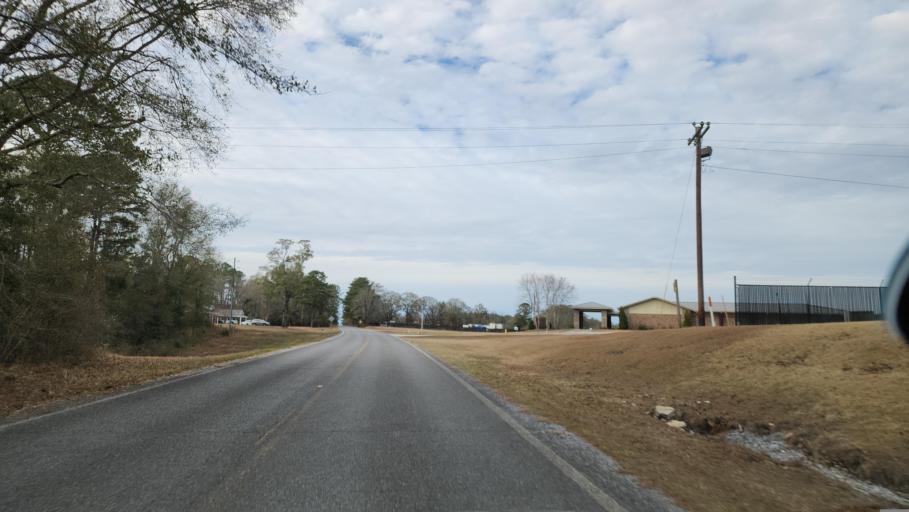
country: US
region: Mississippi
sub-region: Clarke County
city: Stonewall
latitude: 32.2005
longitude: -88.6854
